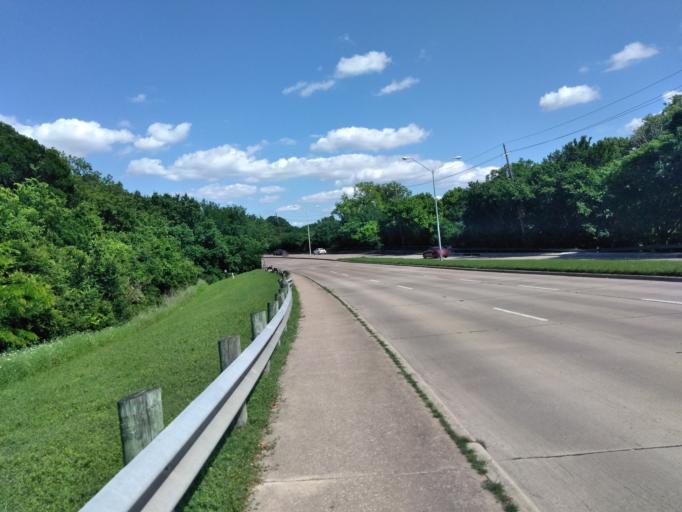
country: US
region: Texas
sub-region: Dallas County
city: Addison
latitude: 32.9986
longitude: -96.8155
